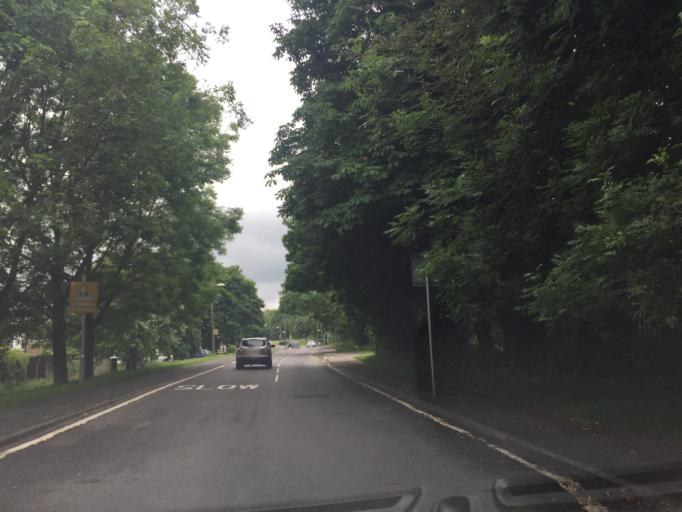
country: GB
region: England
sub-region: Essex
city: Harlow
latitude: 51.7490
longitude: 0.0841
